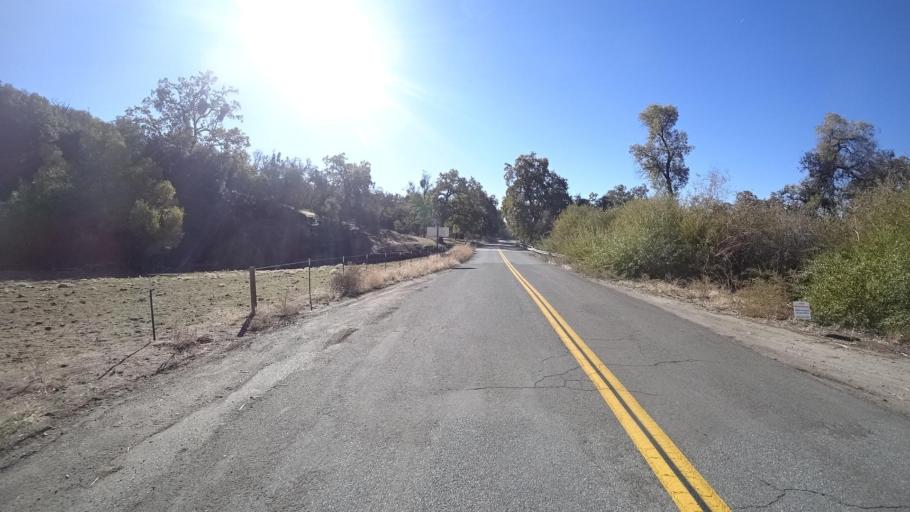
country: US
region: California
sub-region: Kern County
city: Alta Sierra
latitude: 35.7946
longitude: -118.7035
